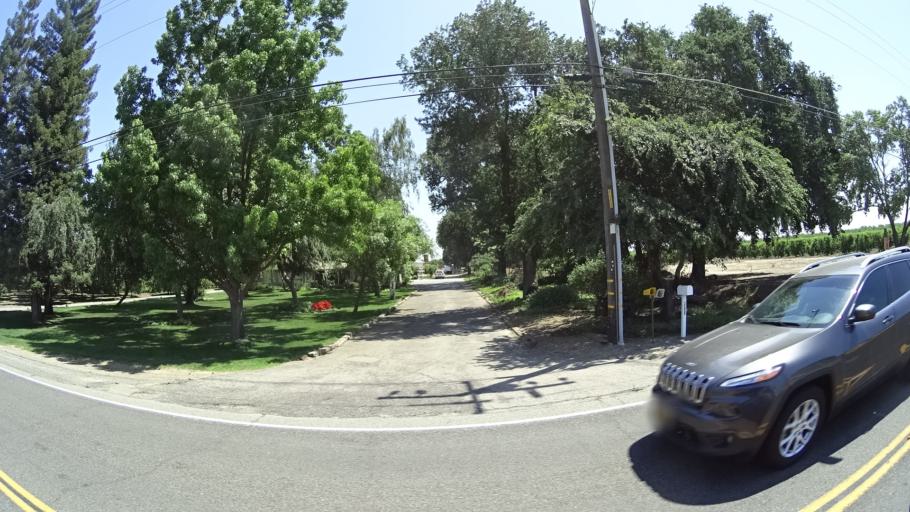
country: US
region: California
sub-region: Fresno County
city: Laton
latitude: 36.4158
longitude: -119.6864
